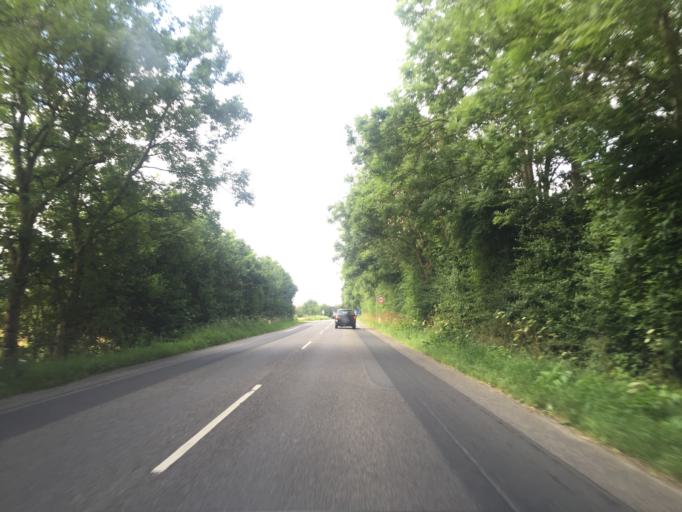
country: DK
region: South Denmark
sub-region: Svendborg Kommune
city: Thuro By
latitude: 55.0956
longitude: 10.7004
